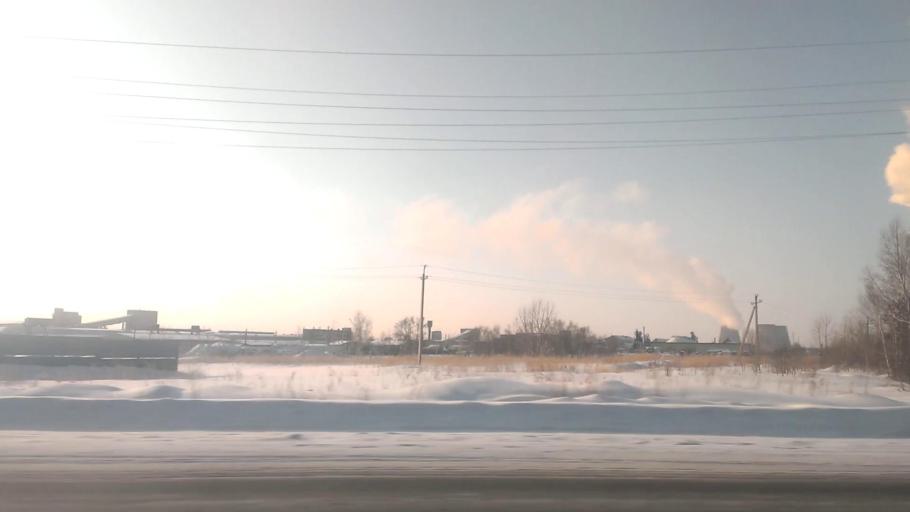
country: RU
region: Altai Krai
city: Novosilikatnyy
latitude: 53.3367
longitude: 83.6437
